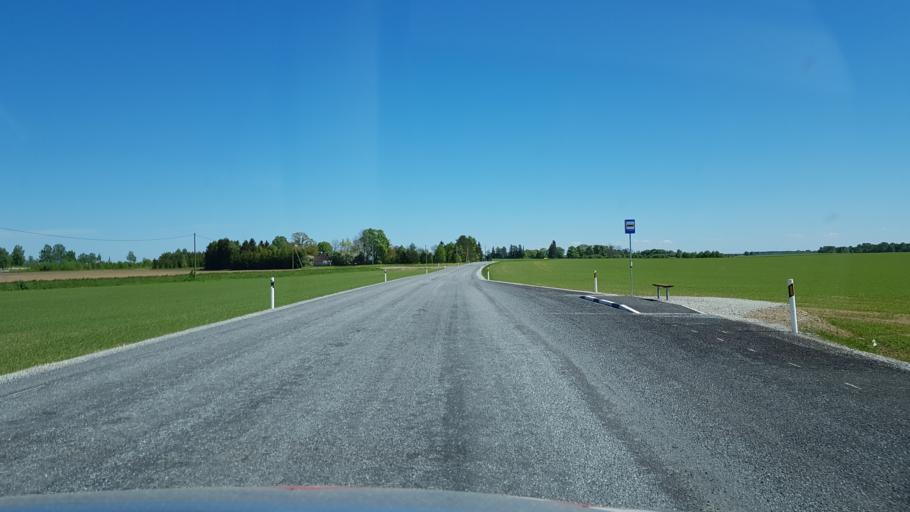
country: EE
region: Laeaene-Virumaa
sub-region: Haljala vald
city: Haljala
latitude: 59.4279
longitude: 26.2125
